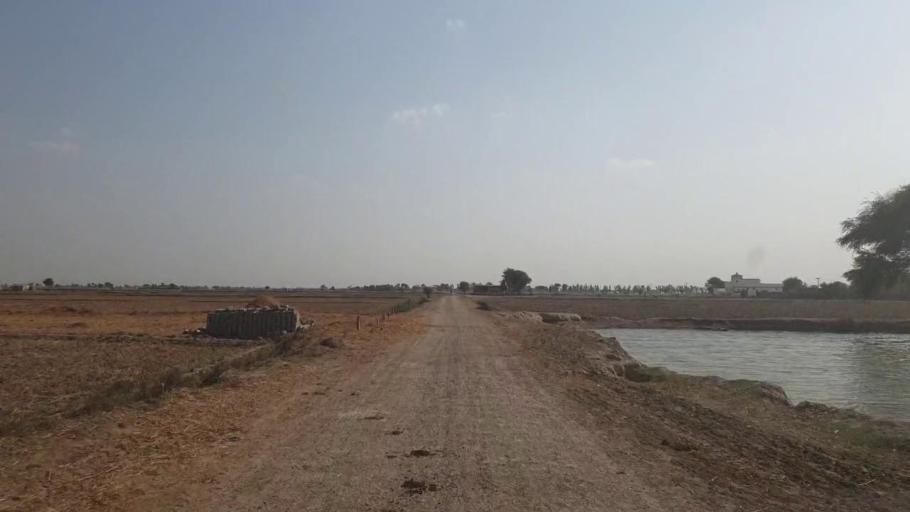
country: PK
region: Sindh
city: Kario
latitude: 24.5553
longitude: 68.5084
